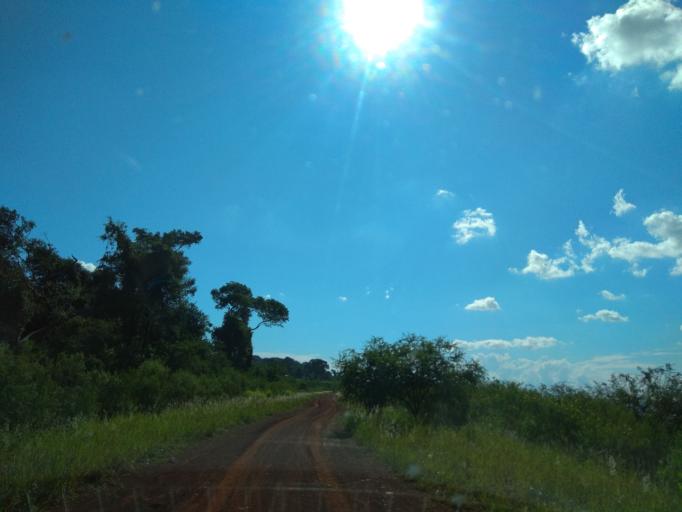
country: AR
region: Misiones
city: Garupa
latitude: -27.4554
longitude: -55.8233
